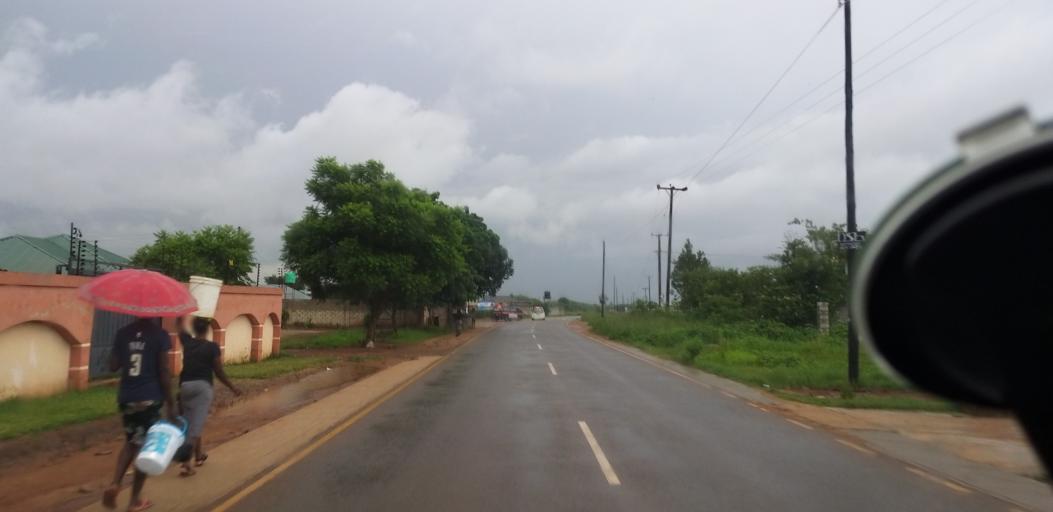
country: ZM
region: Lusaka
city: Lusaka
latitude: -15.4962
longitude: 28.3128
